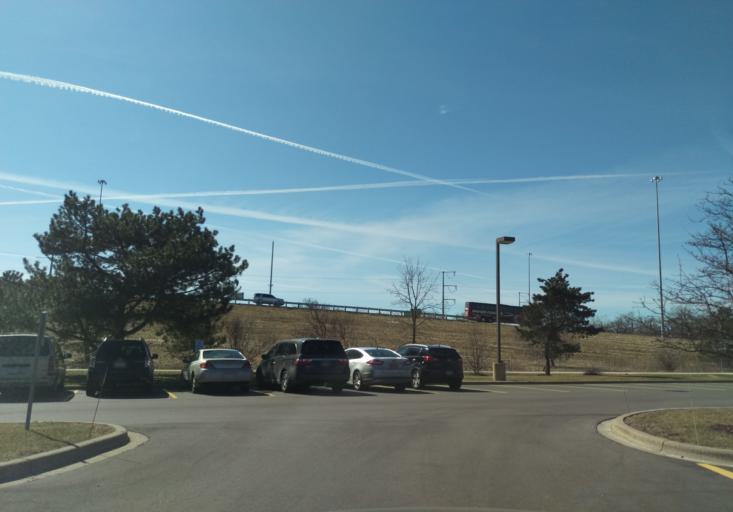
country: US
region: Wisconsin
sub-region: Dane County
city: Monona
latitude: 43.0445
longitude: -89.3684
